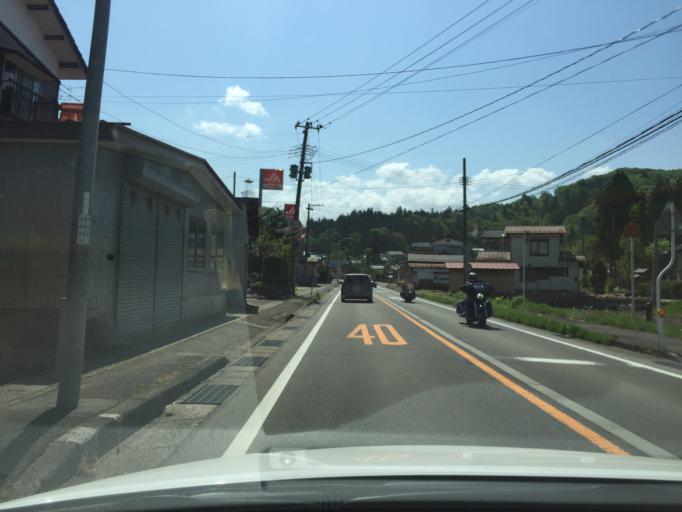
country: JP
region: Niigata
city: Kamo
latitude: 37.6280
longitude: 139.0981
